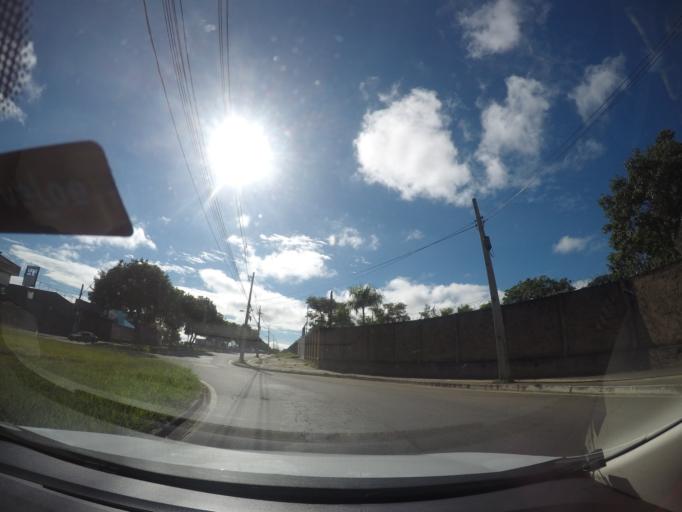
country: BR
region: Goias
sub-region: Goiania
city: Goiania
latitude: -16.6586
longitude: -49.1949
